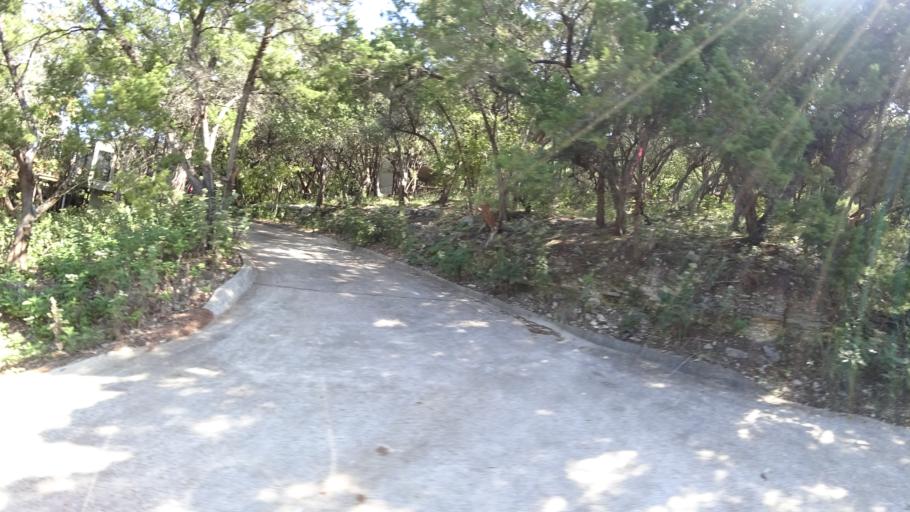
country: US
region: Texas
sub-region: Travis County
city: West Lake Hills
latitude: 30.3053
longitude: -97.8062
